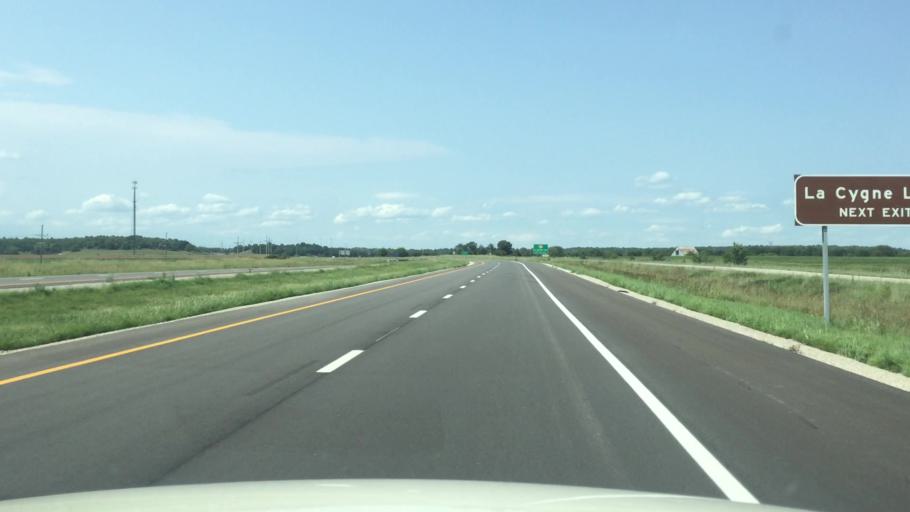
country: US
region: Kansas
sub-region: Linn County
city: La Cygne
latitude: 38.3303
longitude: -94.6773
